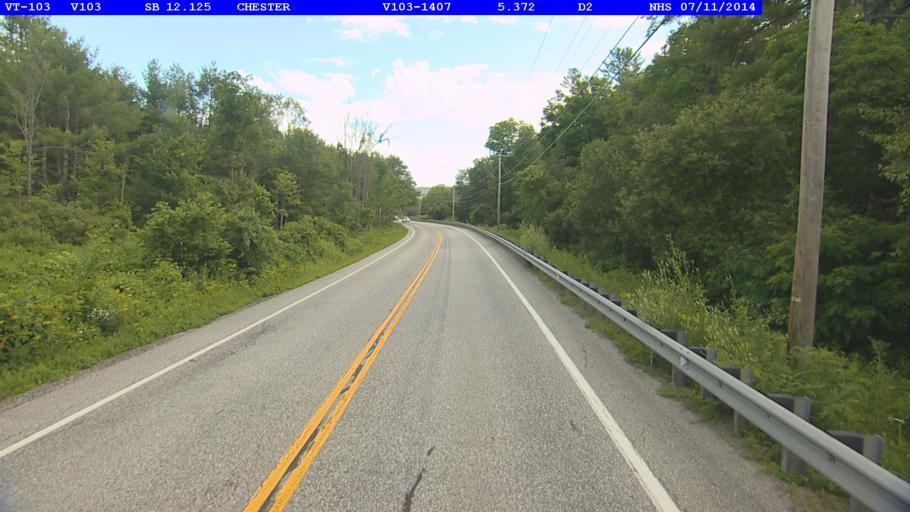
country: US
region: Vermont
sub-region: Windsor County
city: Chester
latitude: 43.2927
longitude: -72.6038
